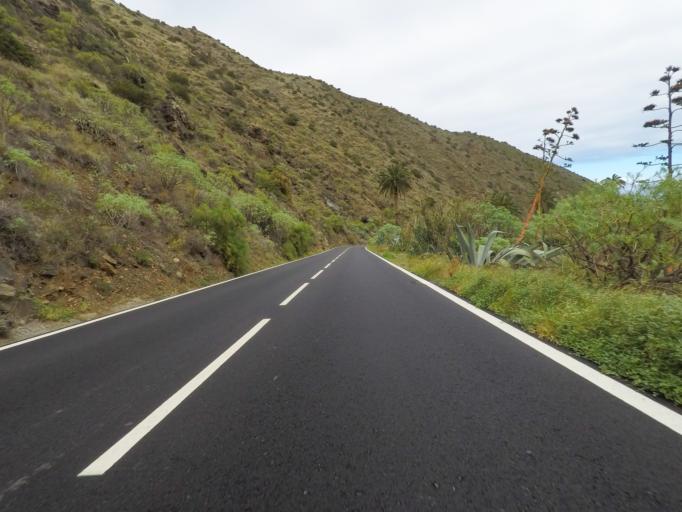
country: ES
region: Canary Islands
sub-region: Provincia de Santa Cruz de Tenerife
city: Vallehermosa
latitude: 28.1922
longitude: -17.2617
